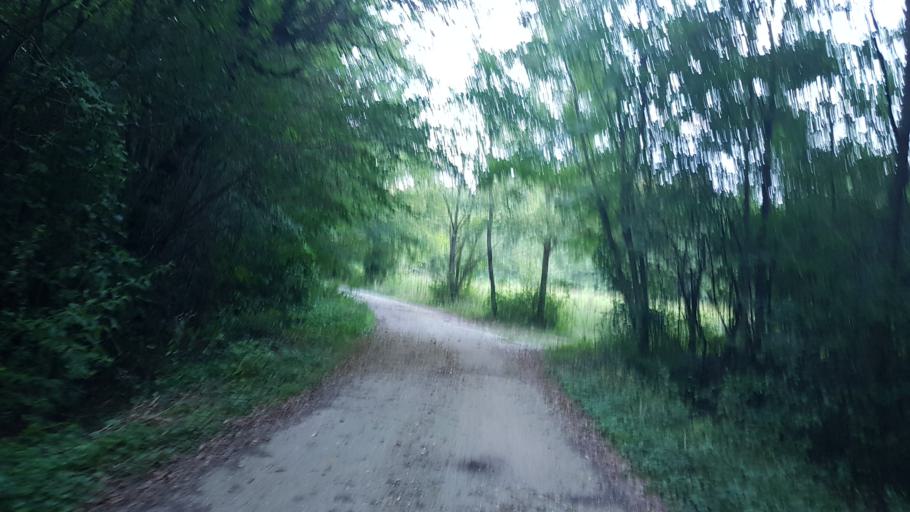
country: IT
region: Friuli Venezia Giulia
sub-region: Provincia di Gorizia
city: Mossa
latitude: 45.9422
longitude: 13.5355
